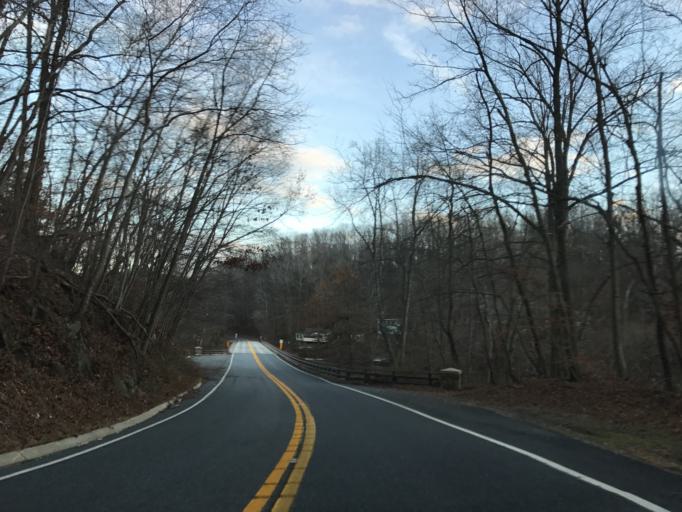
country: US
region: Pennsylvania
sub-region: York County
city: Susquehanna Trails
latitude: 39.6970
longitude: -76.2462
